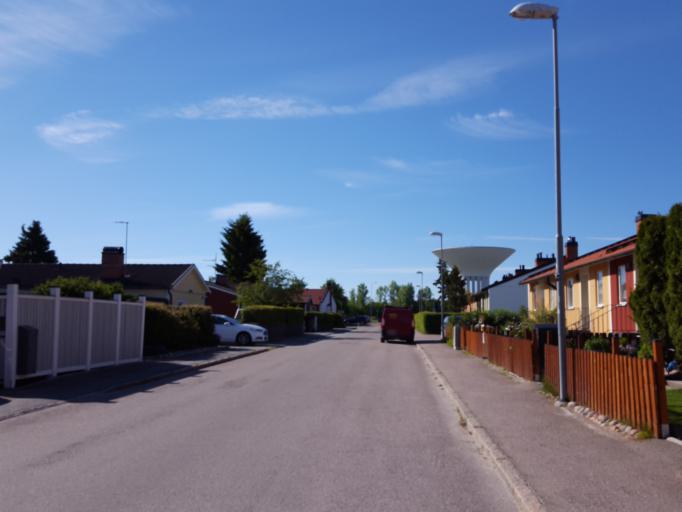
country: SE
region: Uppsala
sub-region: Uppsala Kommun
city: Uppsala
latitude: 59.8600
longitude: 17.6791
